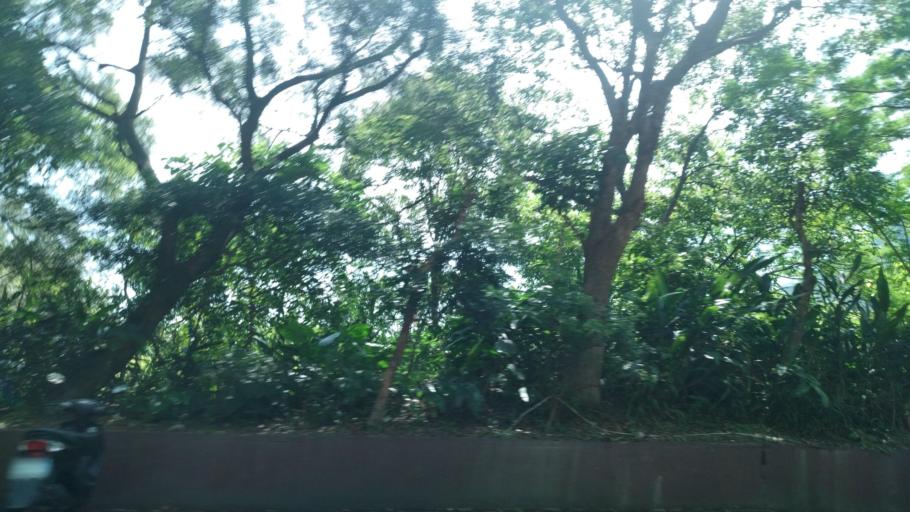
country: TW
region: Taipei
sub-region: Taipei
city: Banqiao
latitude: 24.9418
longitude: 121.5044
